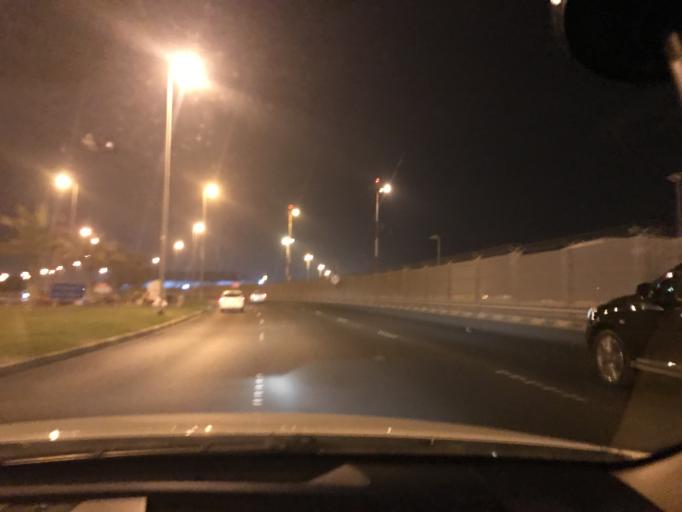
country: BH
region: Muharraq
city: Al Hadd
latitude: 26.2622
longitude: 50.6407
